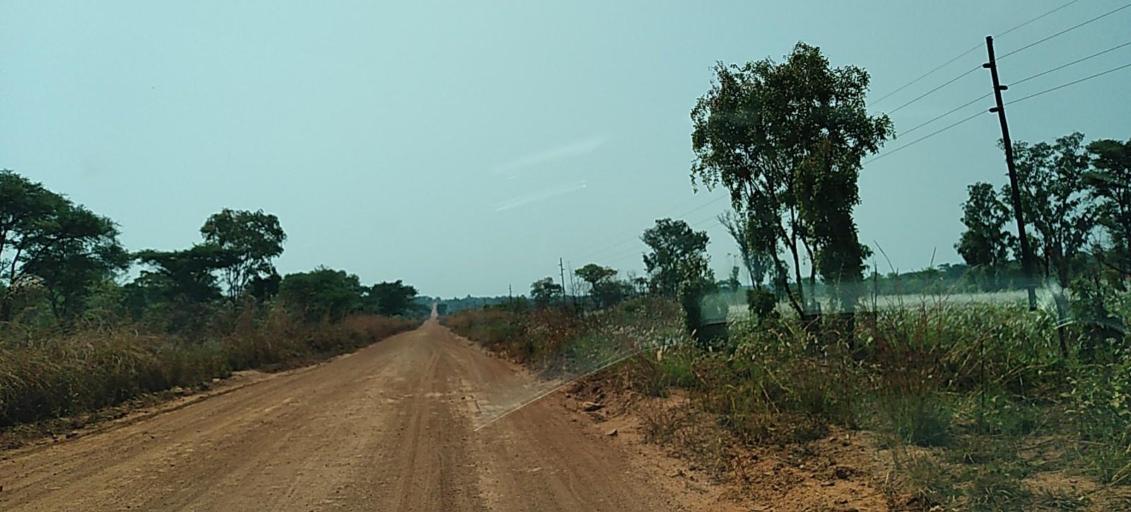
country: ZM
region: North-Western
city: Kansanshi
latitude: -12.0043
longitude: 26.5608
